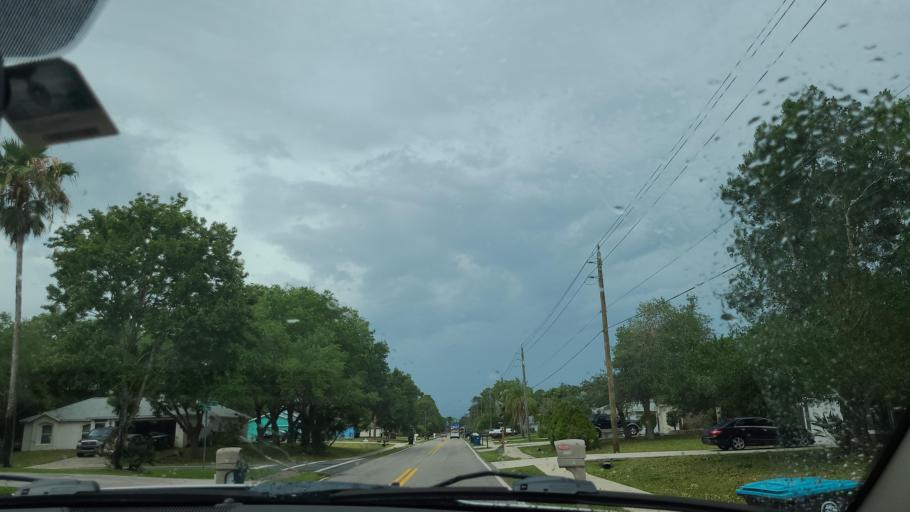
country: US
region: Florida
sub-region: Brevard County
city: Grant-Valkaria
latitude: 27.9517
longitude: -80.6405
